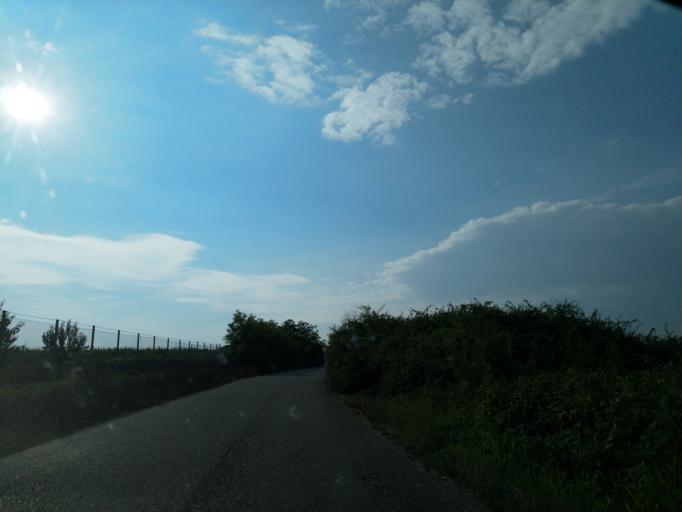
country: RS
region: Central Serbia
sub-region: Pomoravski Okrug
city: Jagodina
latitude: 43.9791
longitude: 21.2301
